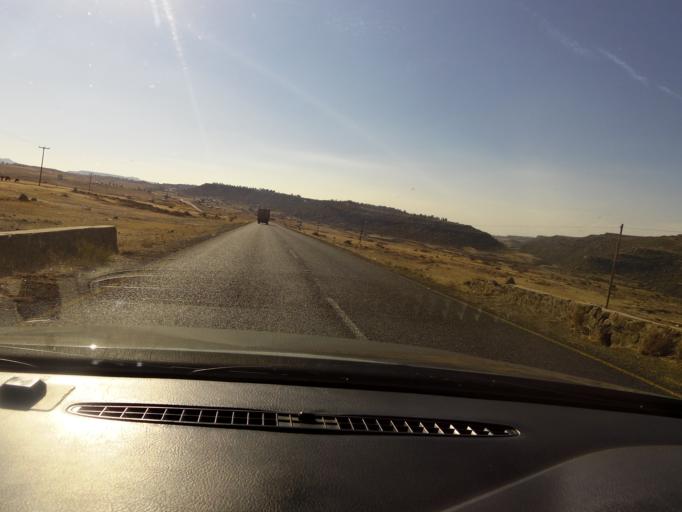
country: LS
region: Mohale's Hoek District
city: Mohale's Hoek
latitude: -30.0583
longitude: 27.4123
